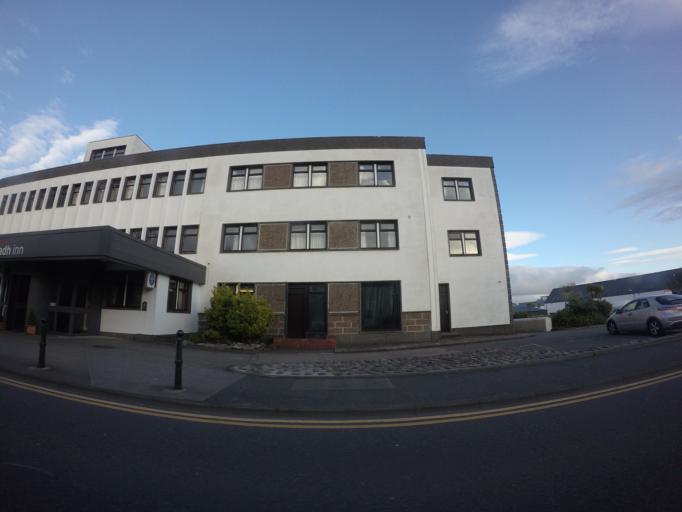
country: GB
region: Scotland
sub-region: Eilean Siar
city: Stornoway
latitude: 58.2083
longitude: -6.3822
